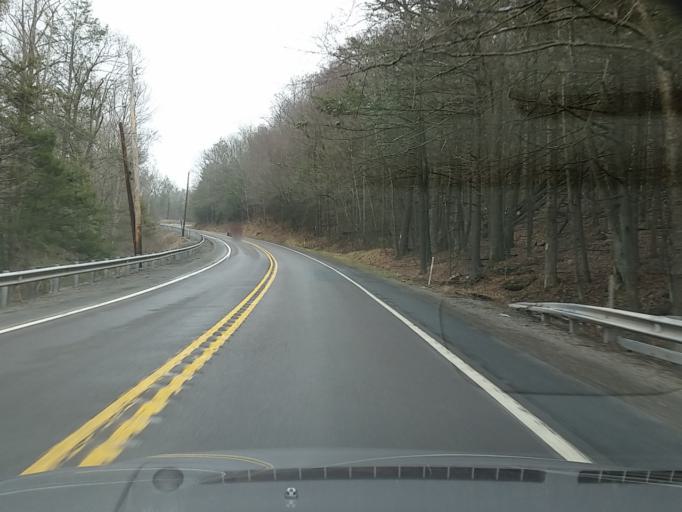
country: US
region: Pennsylvania
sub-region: Sullivan County
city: Laporte
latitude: 41.2770
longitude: -76.3690
